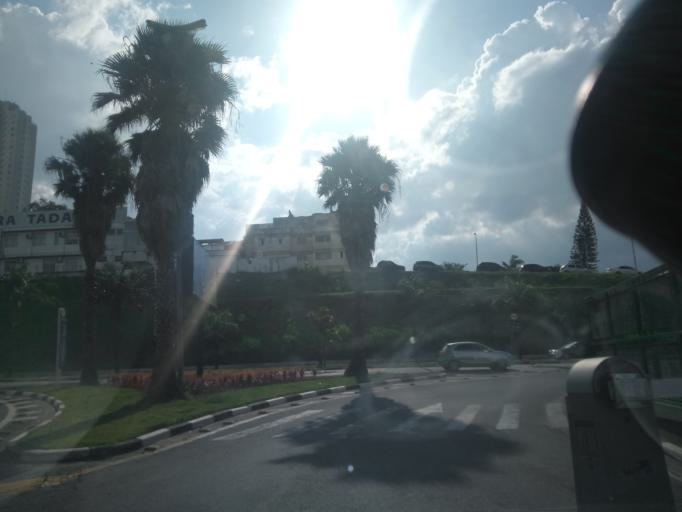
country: BR
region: Sao Paulo
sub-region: Taboao Da Serra
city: Taboao da Serra
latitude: -23.6143
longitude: -46.7775
